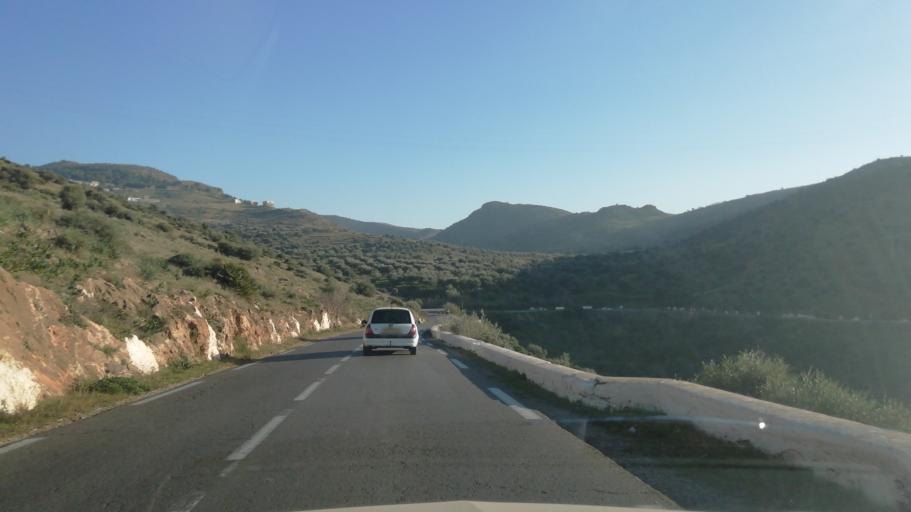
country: DZ
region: Tlemcen
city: Beni Mester
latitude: 34.8516
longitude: -1.4515
